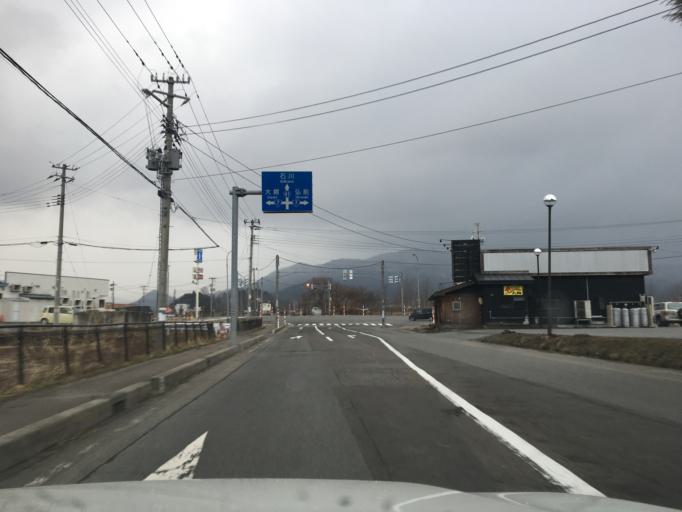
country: JP
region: Aomori
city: Hirosaki
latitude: 40.5567
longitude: 140.5456
